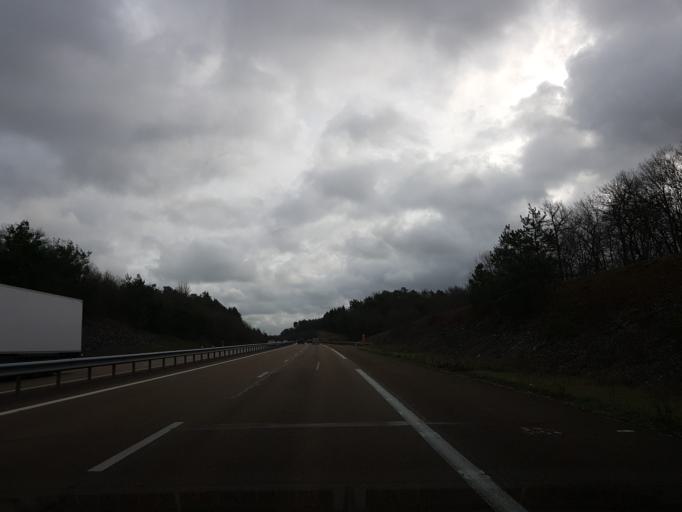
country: FR
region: Champagne-Ardenne
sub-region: Departement de la Haute-Marne
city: Chamarandes-Choignes
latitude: 48.0142
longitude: 5.0996
